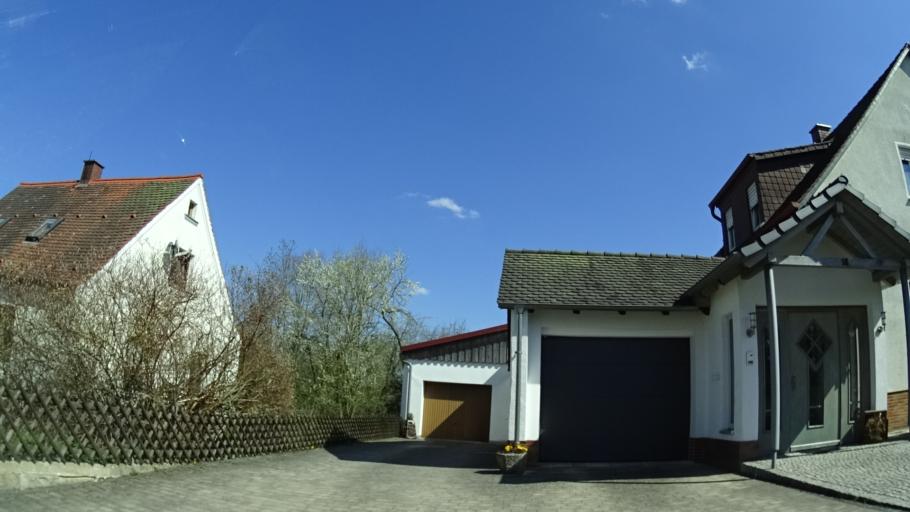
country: DE
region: Bavaria
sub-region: Upper Palatinate
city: Edelsfeld
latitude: 49.5467
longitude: 11.7258
